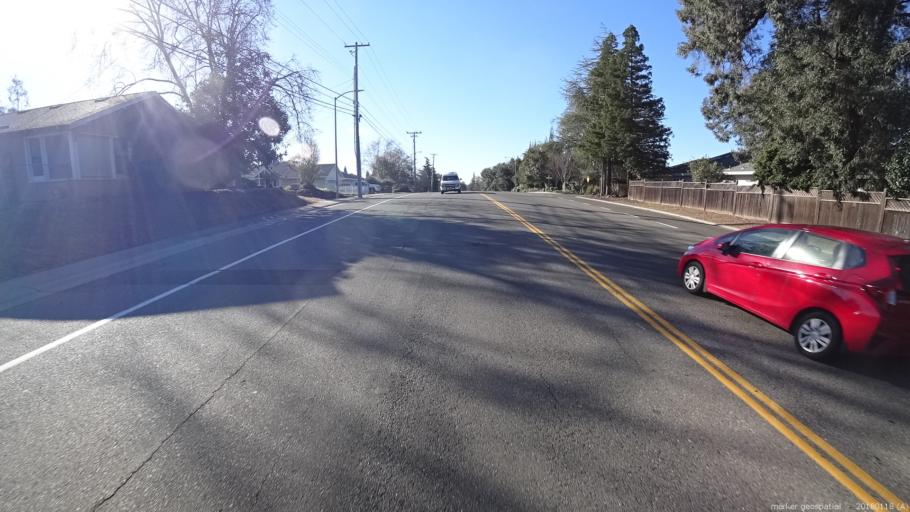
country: US
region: California
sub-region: Sacramento County
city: Orangevale
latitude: 38.6766
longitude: -121.2443
